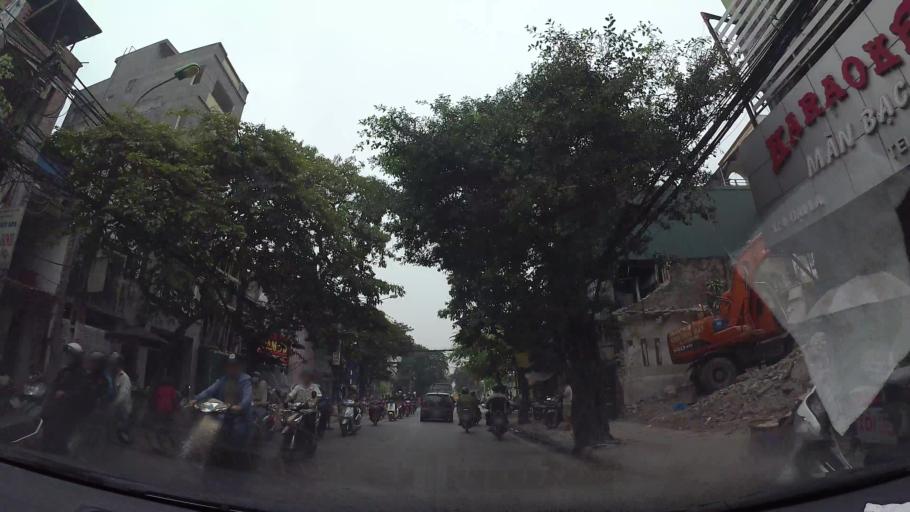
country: VN
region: Ha Noi
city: Hai BaTrung
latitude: 20.9964
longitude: 105.8462
